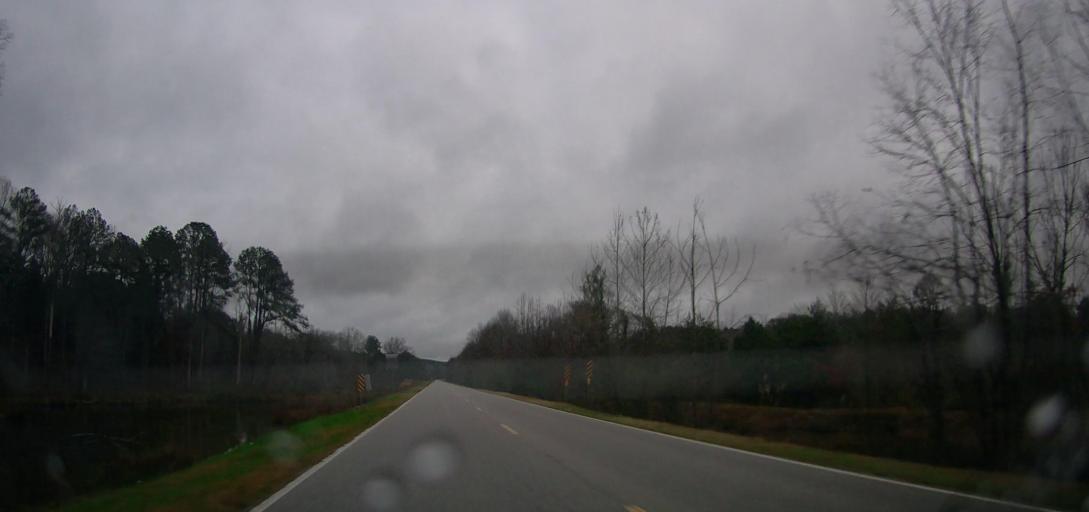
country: US
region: Alabama
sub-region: Bibb County
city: Centreville
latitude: 32.9257
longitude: -87.0442
